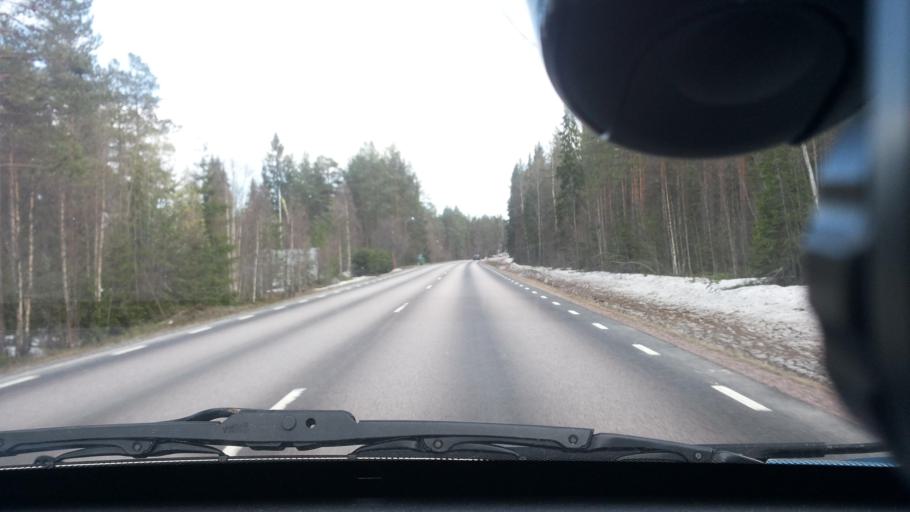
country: SE
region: Norrbotten
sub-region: Lulea Kommun
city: Gammelstad
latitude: 65.5979
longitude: 21.9919
